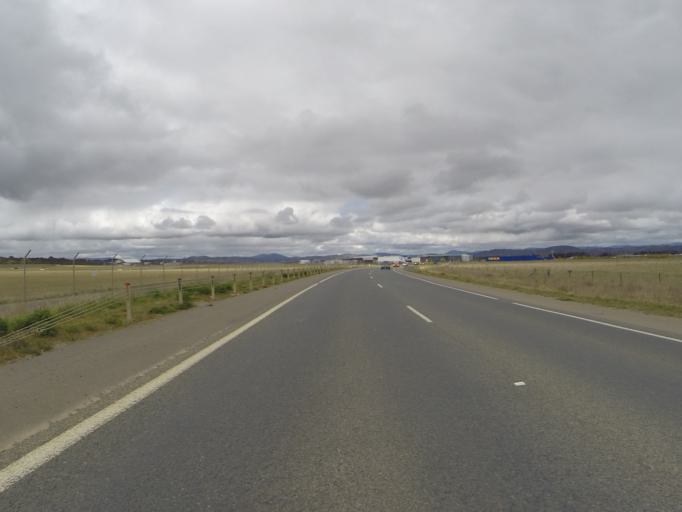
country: AU
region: Australian Capital Territory
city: Canberra
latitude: -35.2874
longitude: 149.1934
